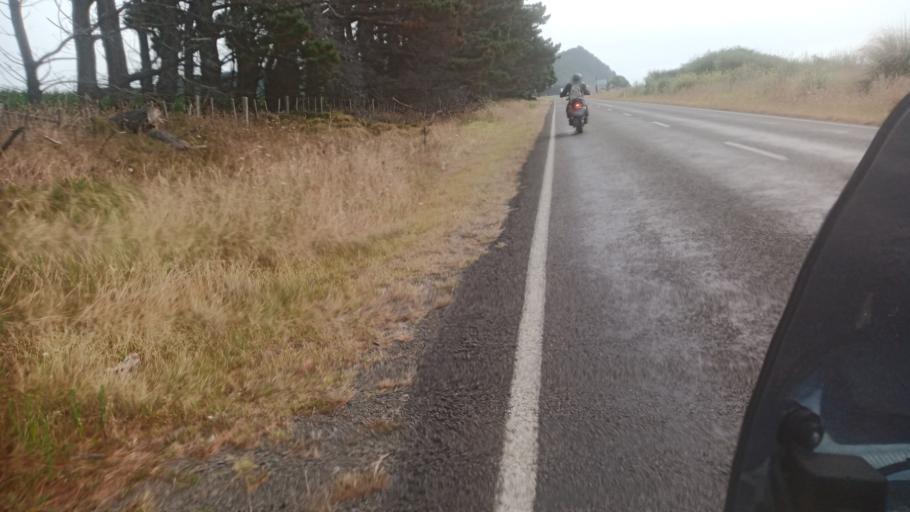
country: NZ
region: Bay of Plenty
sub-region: Opotiki District
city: Opotiki
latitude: -37.9260
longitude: 177.5179
